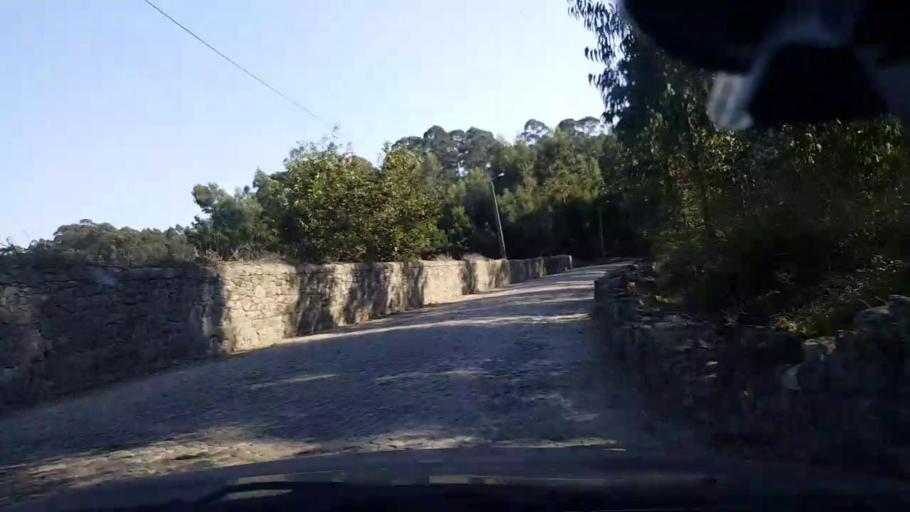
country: PT
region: Porto
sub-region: Vila do Conde
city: Arvore
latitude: 41.3569
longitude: -8.7024
